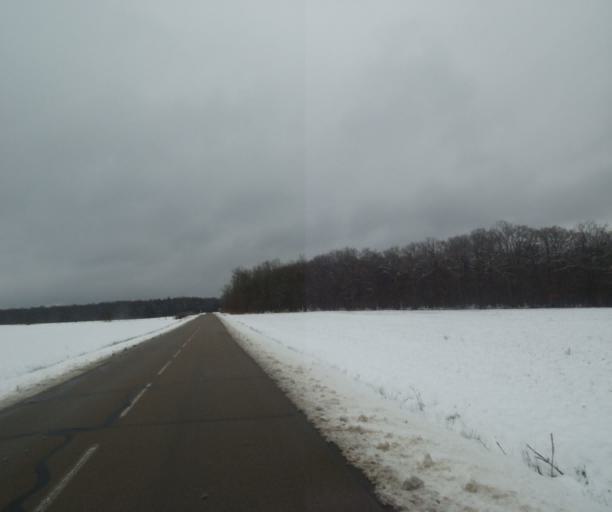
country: FR
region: Champagne-Ardenne
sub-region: Departement de la Haute-Marne
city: Laneuville-a-Remy
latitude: 48.4366
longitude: 4.8563
